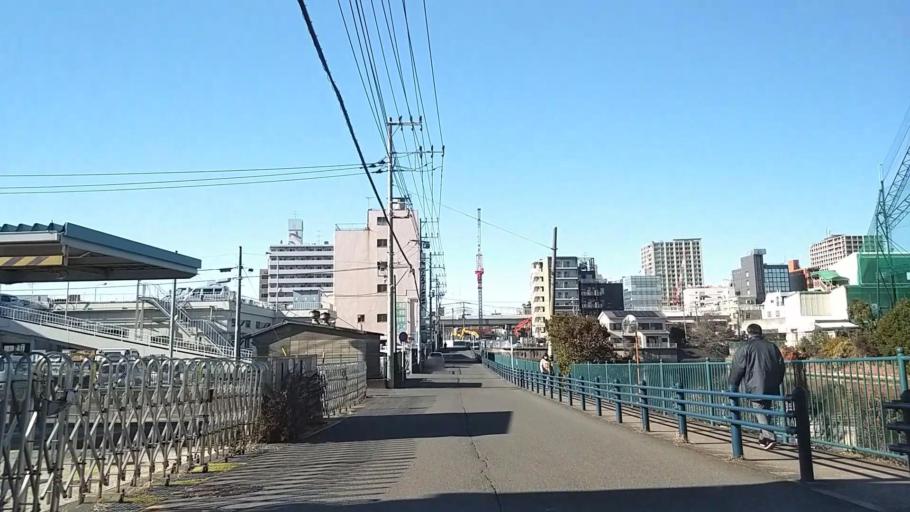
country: JP
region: Kanagawa
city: Yokohama
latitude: 35.4732
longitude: 139.6366
